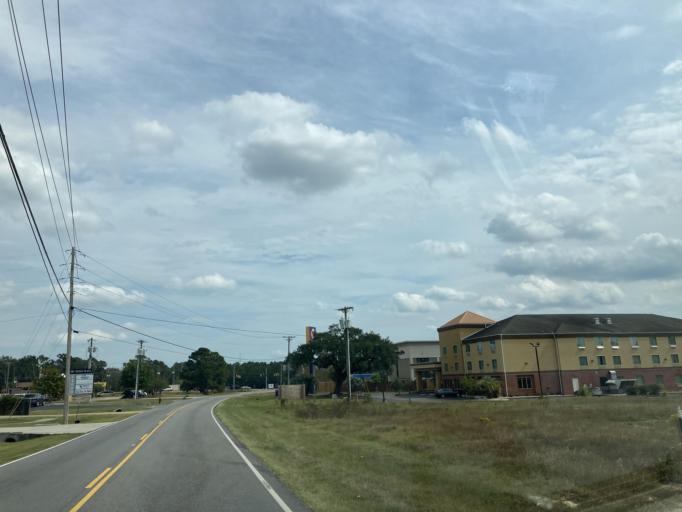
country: US
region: Mississippi
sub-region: Jackson County
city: Gulf Hills
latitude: 30.4504
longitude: -88.8441
